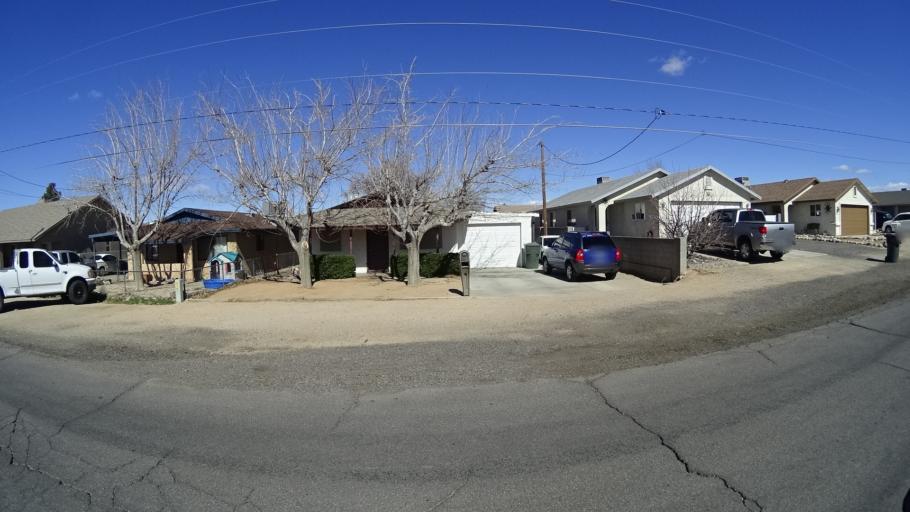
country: US
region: Arizona
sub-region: Mohave County
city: Kingman
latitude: 35.1960
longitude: -114.0169
